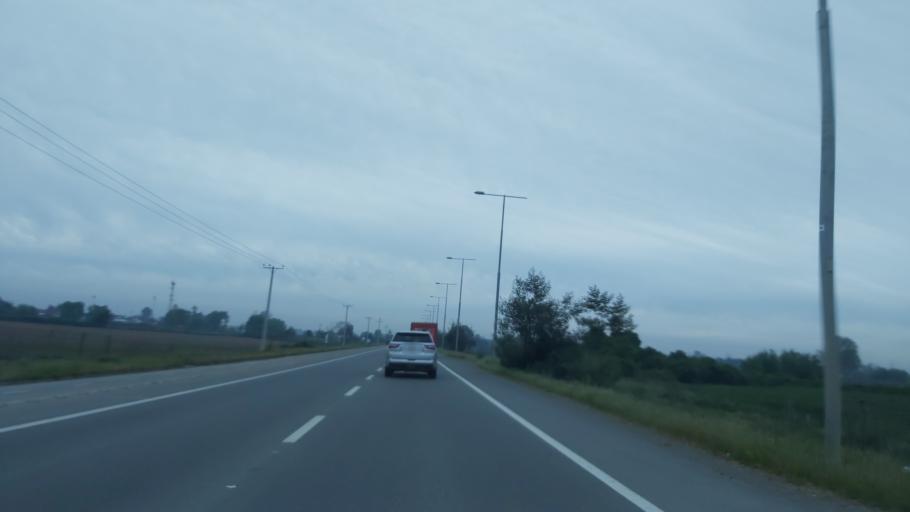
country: CL
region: Maule
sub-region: Provincia de Linares
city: Linares
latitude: -35.8278
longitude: -71.6064
